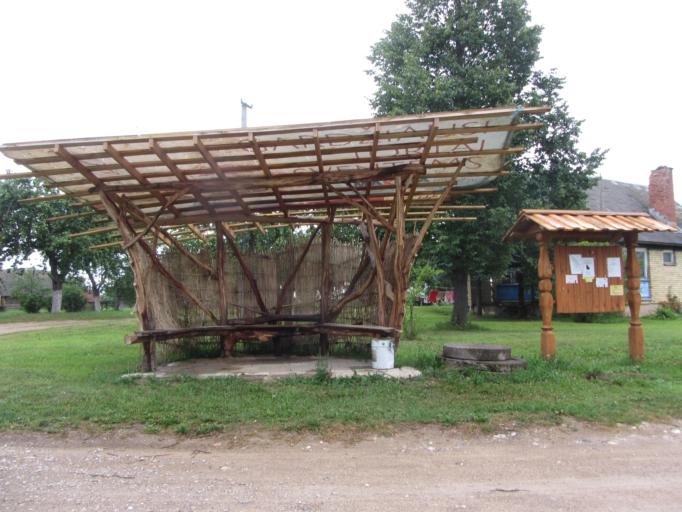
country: LT
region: Utenos apskritis
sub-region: Utena
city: Utena
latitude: 55.6150
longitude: 25.8912
